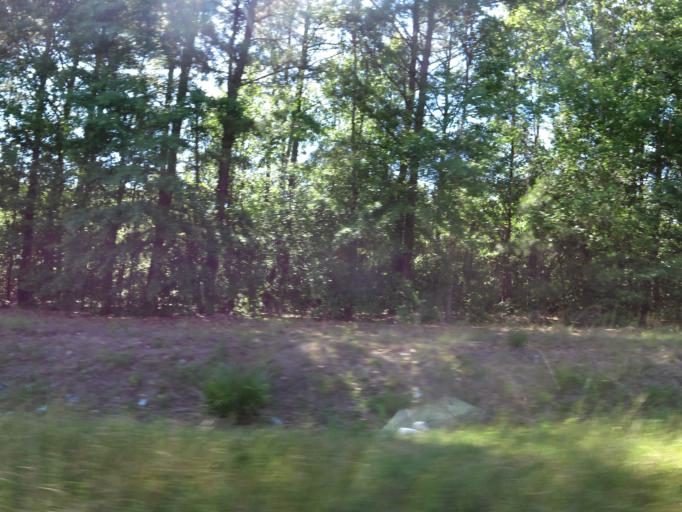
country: US
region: South Carolina
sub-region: Bamberg County
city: Denmark
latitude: 33.2841
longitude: -81.1499
